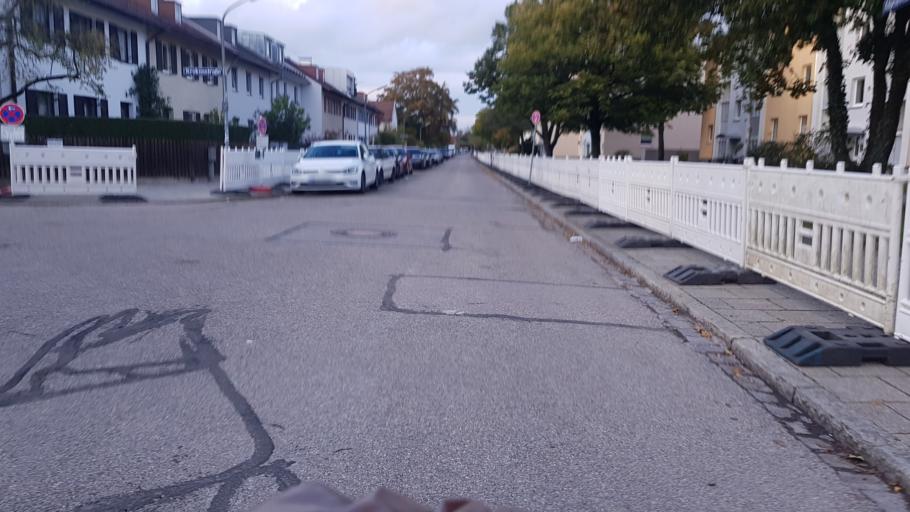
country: DE
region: Bavaria
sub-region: Upper Bavaria
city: Pasing
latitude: 48.1251
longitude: 11.4899
